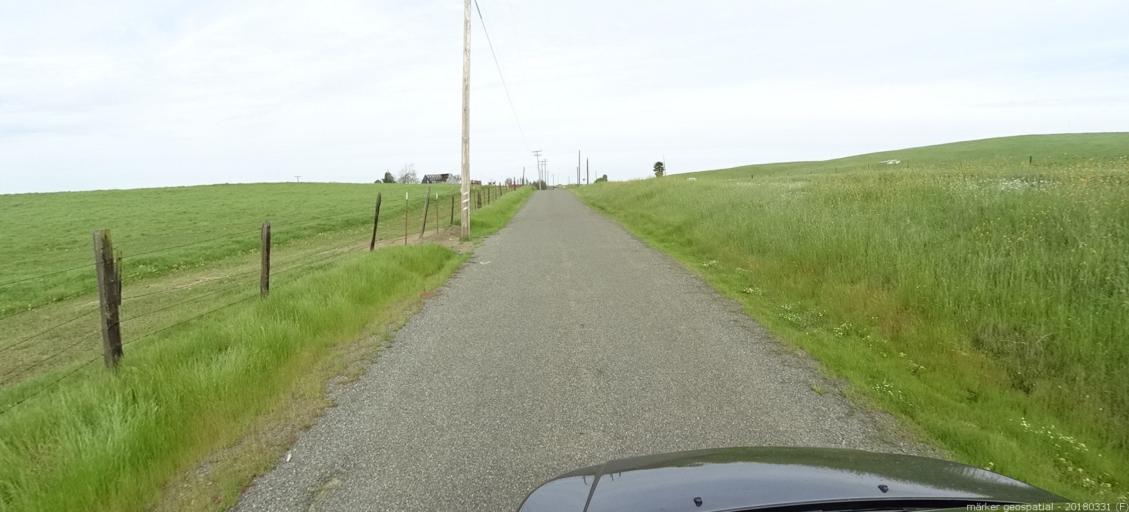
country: US
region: California
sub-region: El Dorado County
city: El Dorado Hills
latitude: 38.6253
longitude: -121.0894
